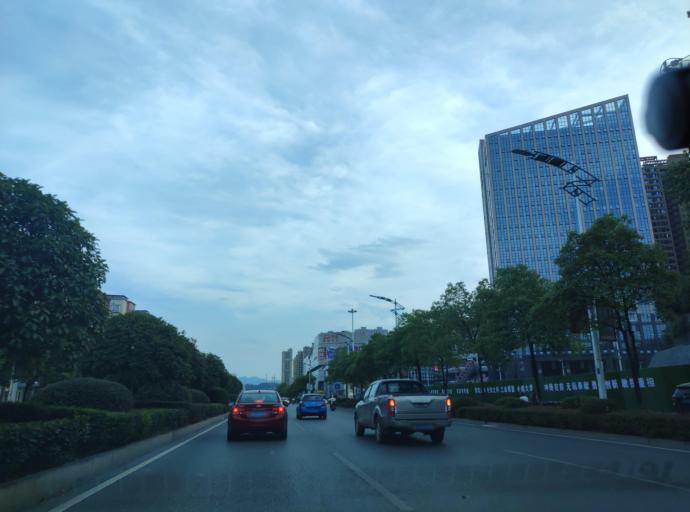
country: CN
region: Jiangxi Sheng
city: Pingxiang
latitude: 27.6384
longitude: 113.8703
